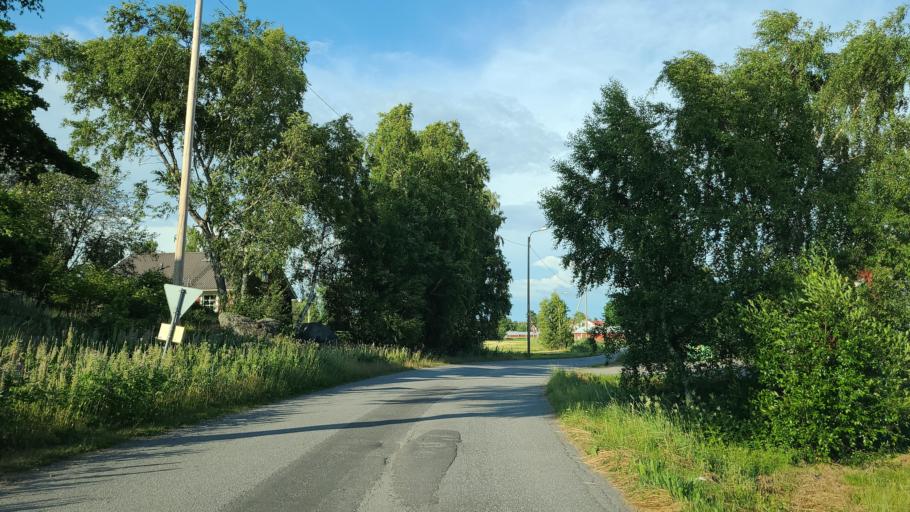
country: FI
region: Ostrobothnia
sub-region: Vaasa
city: Replot
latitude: 63.3445
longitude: 21.3286
